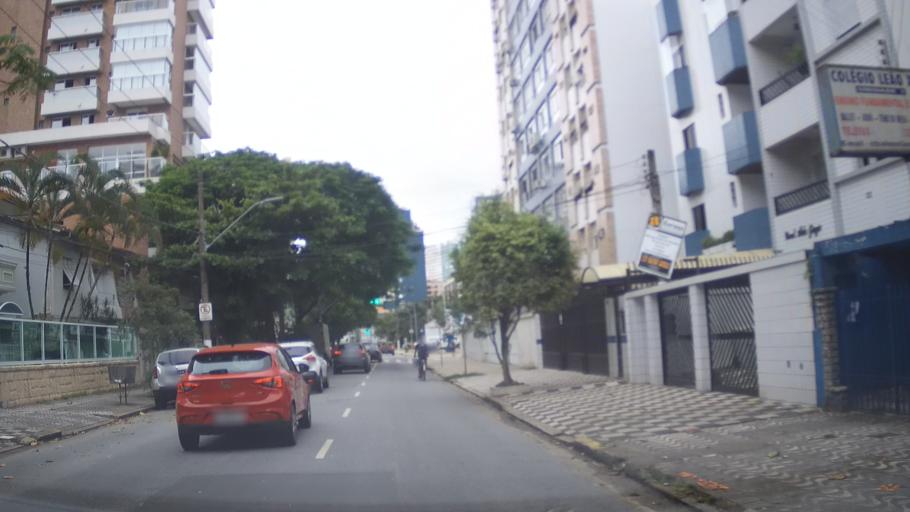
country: BR
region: Sao Paulo
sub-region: Santos
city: Santos
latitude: -23.9720
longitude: -46.3187
